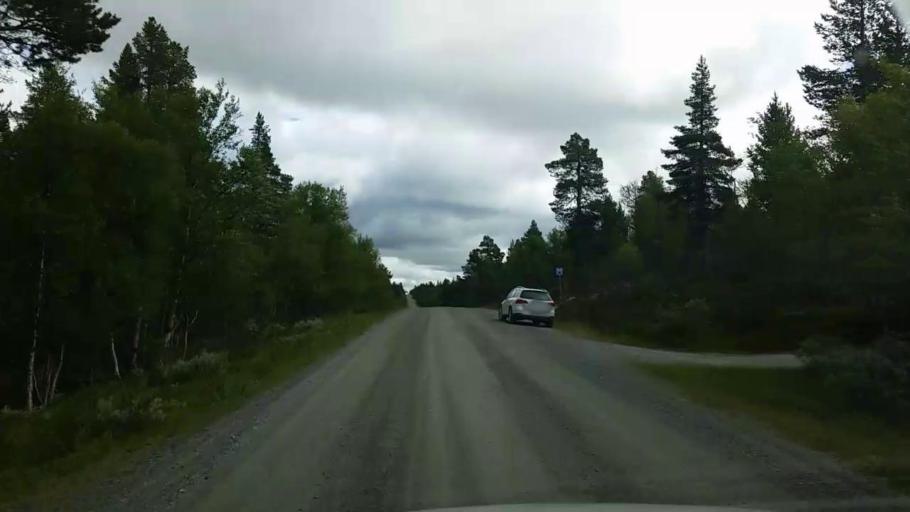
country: NO
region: Hedmark
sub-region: Engerdal
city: Engerdal
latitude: 62.3454
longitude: 12.5976
